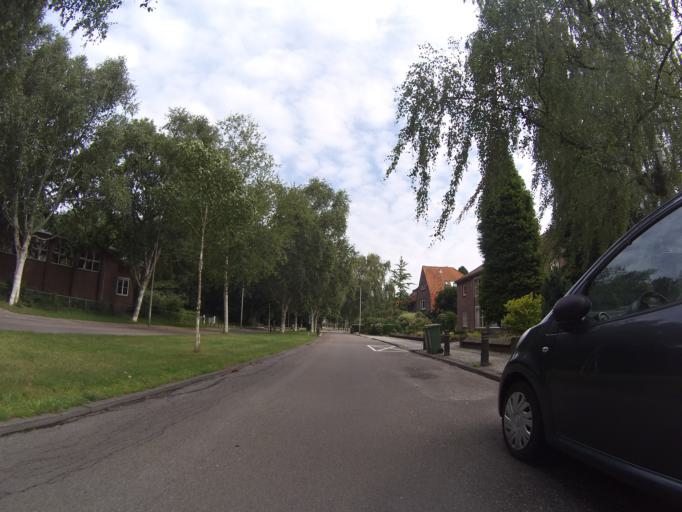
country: NL
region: Utrecht
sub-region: Gemeente Amersfoort
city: Amersfoort
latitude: 52.1388
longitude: 5.3743
